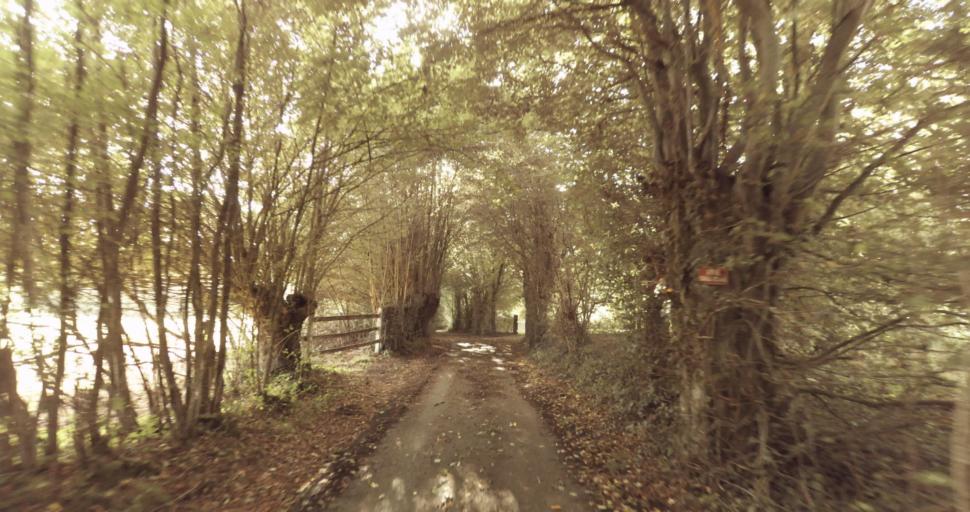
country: FR
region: Lower Normandy
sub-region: Departement de l'Orne
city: Sainte-Gauburge-Sainte-Colombe
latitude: 48.7152
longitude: 0.4057
